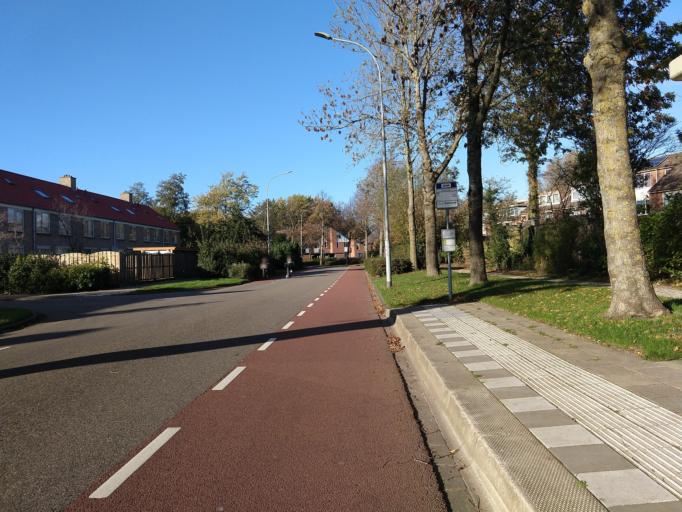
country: NL
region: Zeeland
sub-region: Gemeente Middelburg
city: Middelburg
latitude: 51.4875
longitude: 3.6279
